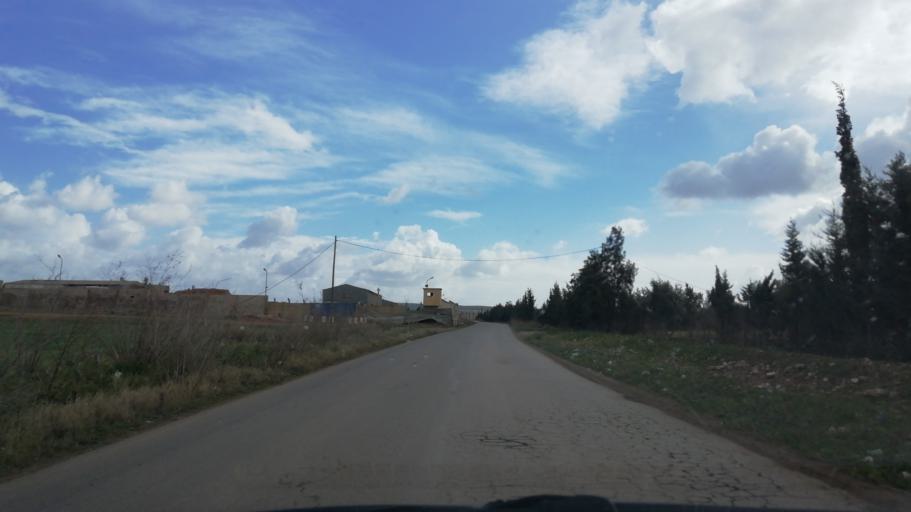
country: DZ
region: Oran
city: Sidi ech Chahmi
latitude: 35.6345
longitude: -0.5336
